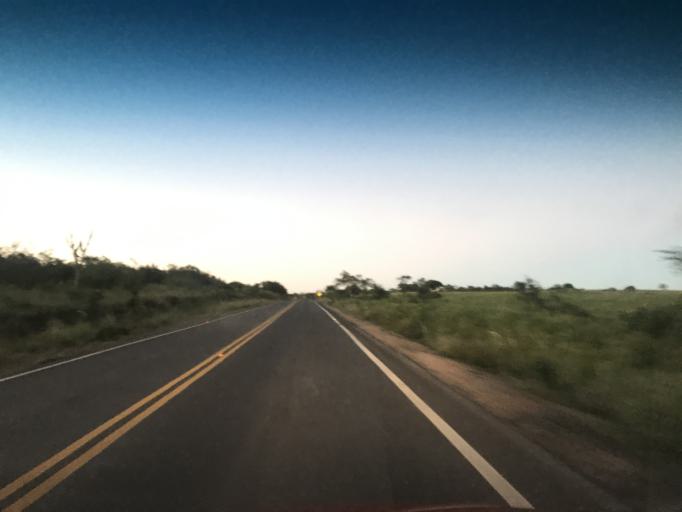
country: BR
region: Bahia
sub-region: Castro Alves
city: Castro Alves
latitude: -12.7519
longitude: -39.4066
